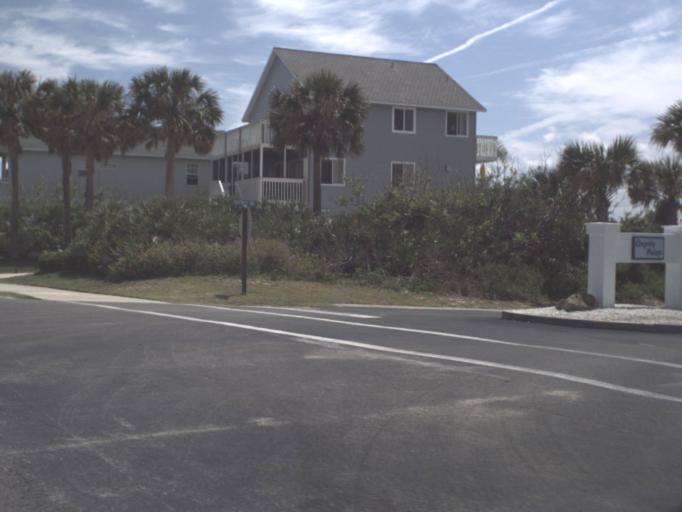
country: US
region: Florida
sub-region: Flagler County
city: Flagler Beach
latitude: 29.5152
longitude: -81.1447
